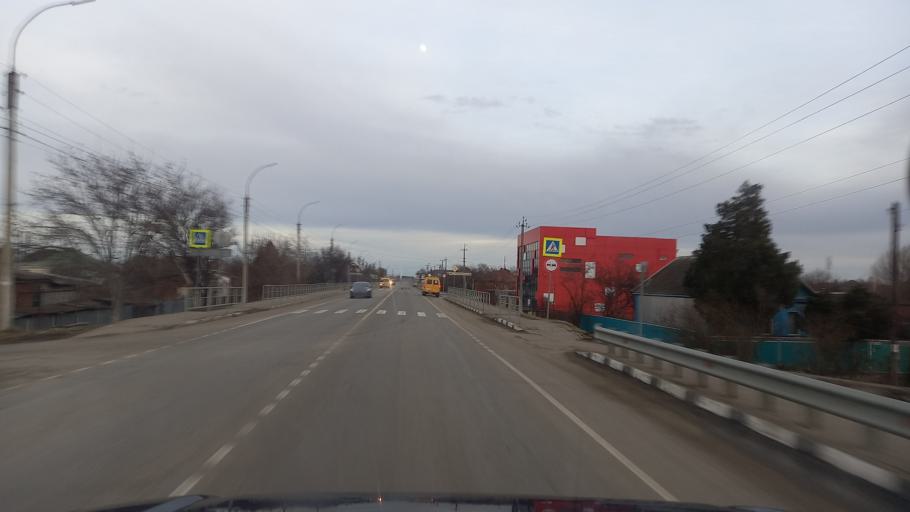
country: RU
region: Krasnodarskiy
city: Belorechensk
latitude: 44.7717
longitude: 39.8969
